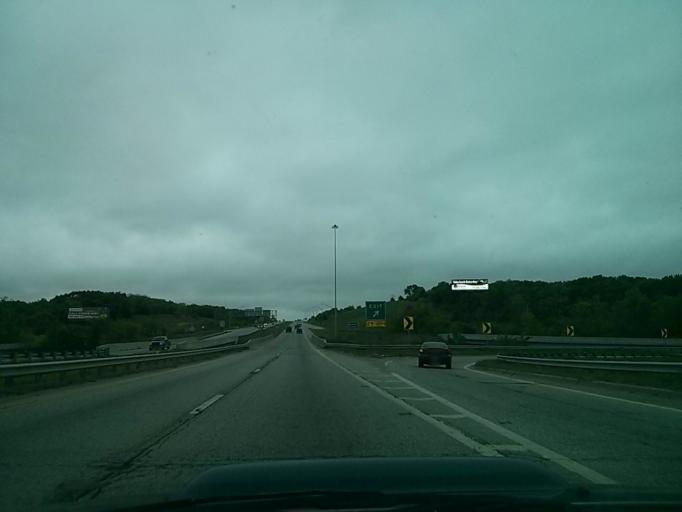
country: US
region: Oklahoma
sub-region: Tulsa County
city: Oakhurst
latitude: 36.0883
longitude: -96.0068
